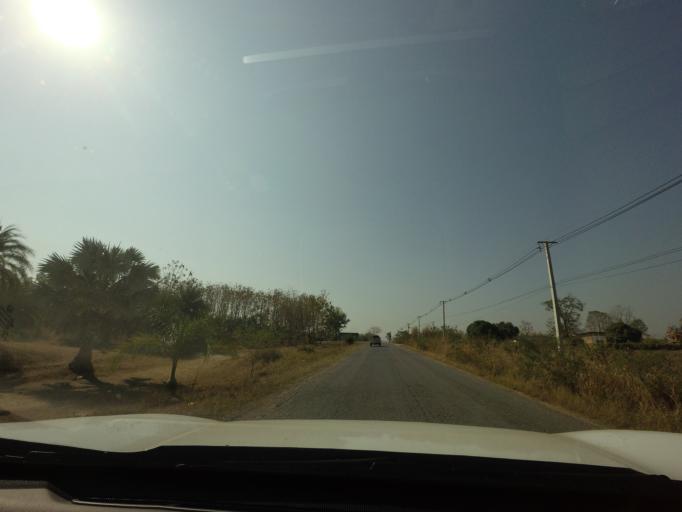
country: TH
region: Nakhon Ratchasima
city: Pak Chong
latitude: 14.6290
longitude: 101.4865
